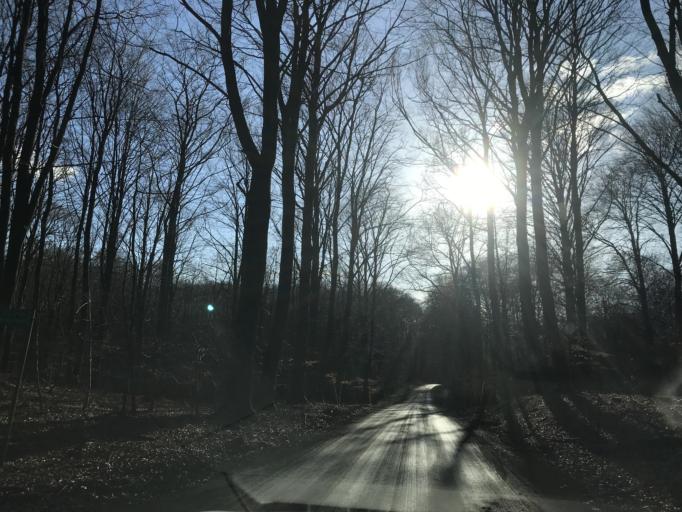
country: SE
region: Skane
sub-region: Ystads Kommun
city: Ystad
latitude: 55.5605
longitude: 13.8241
